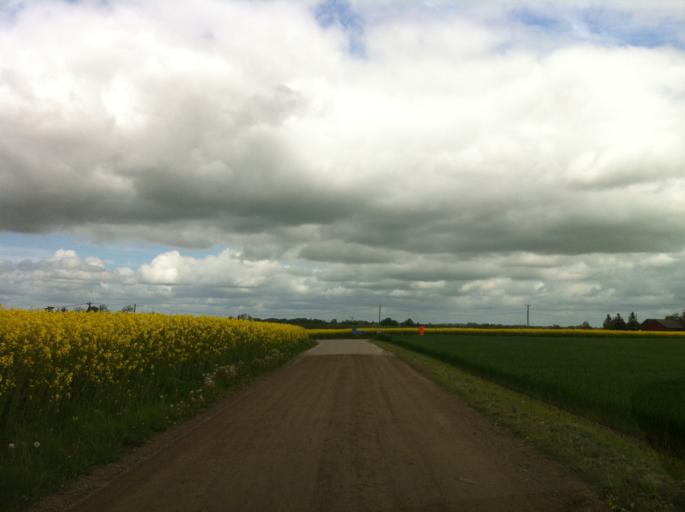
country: SE
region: Skane
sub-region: Svalovs Kommun
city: Teckomatorp
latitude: 55.8435
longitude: 13.0734
